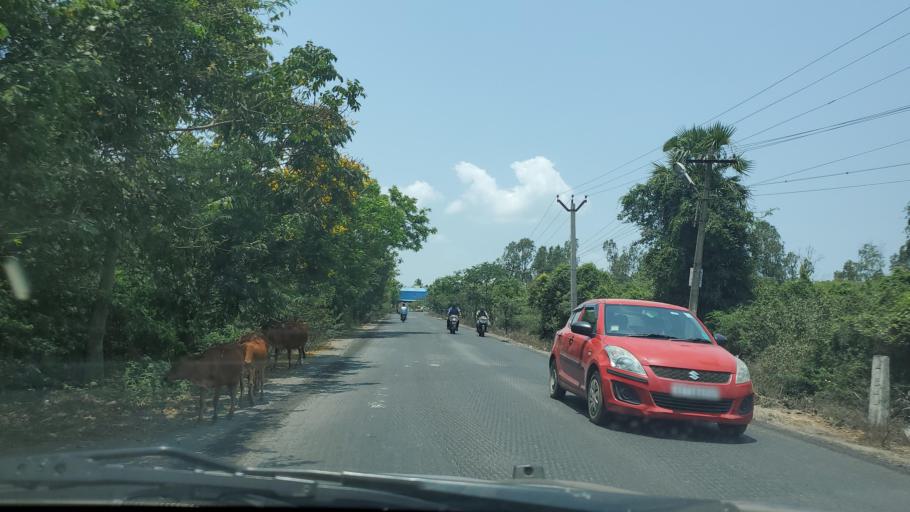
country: IN
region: Tamil Nadu
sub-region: Kancheepuram
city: Vengavasal
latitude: 12.8765
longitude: 80.1706
